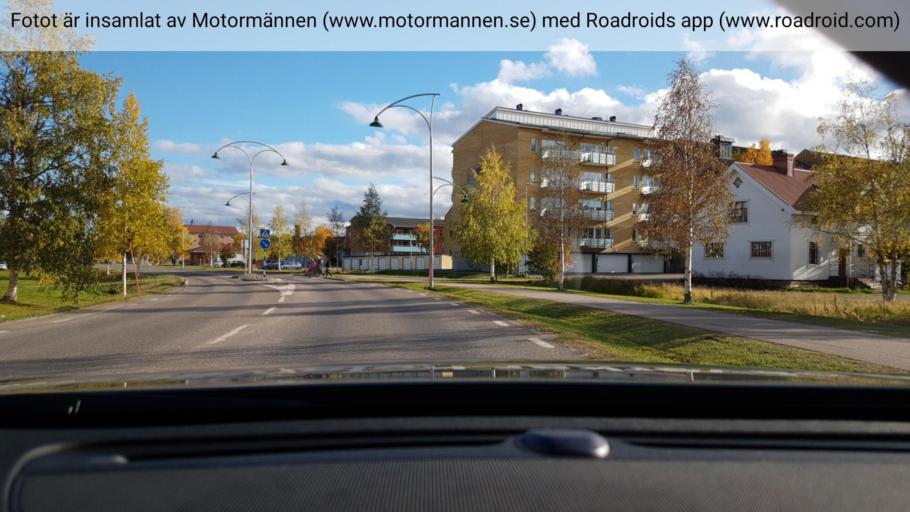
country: SE
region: Norrbotten
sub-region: Gallivare Kommun
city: Gaellivare
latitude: 67.1374
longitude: 20.6608
